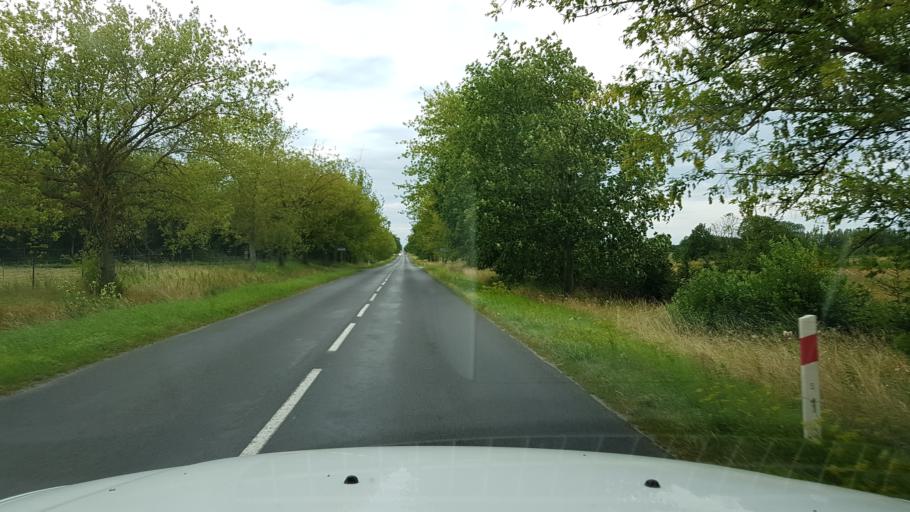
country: PL
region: West Pomeranian Voivodeship
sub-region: Powiat kolobrzeski
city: Kolobrzeg
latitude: 54.1476
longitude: 15.6425
